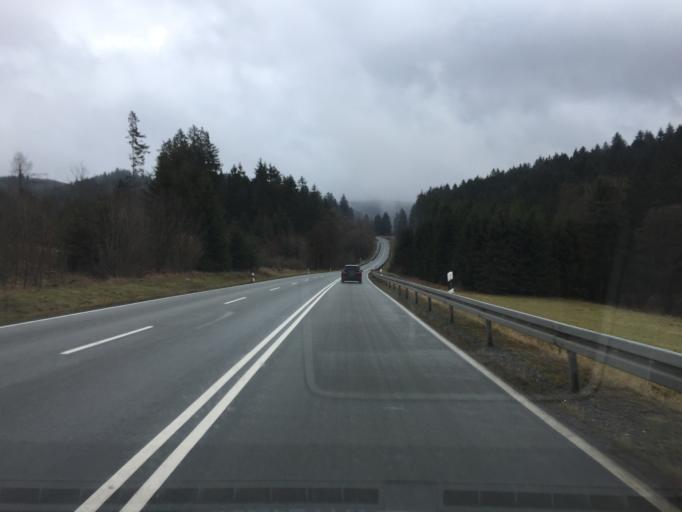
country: DE
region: North Rhine-Westphalia
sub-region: Regierungsbezirk Arnsberg
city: Medebach
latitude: 51.2144
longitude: 8.6297
